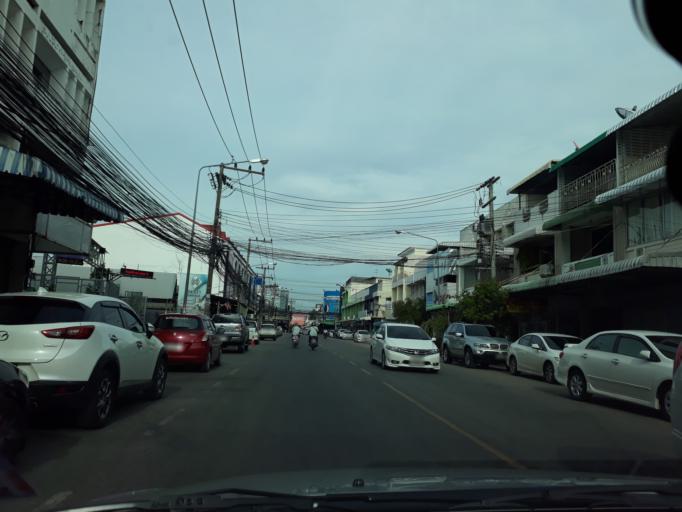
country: TH
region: Khon Kaen
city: Khon Kaen
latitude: 16.4246
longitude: 102.8335
